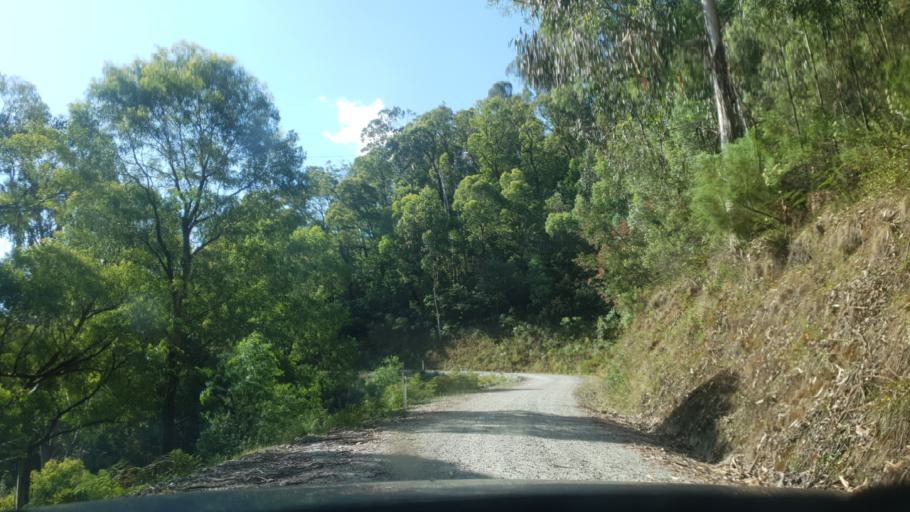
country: AU
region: Victoria
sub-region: Alpine
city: Mount Beauty
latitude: -36.7554
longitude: 147.1871
